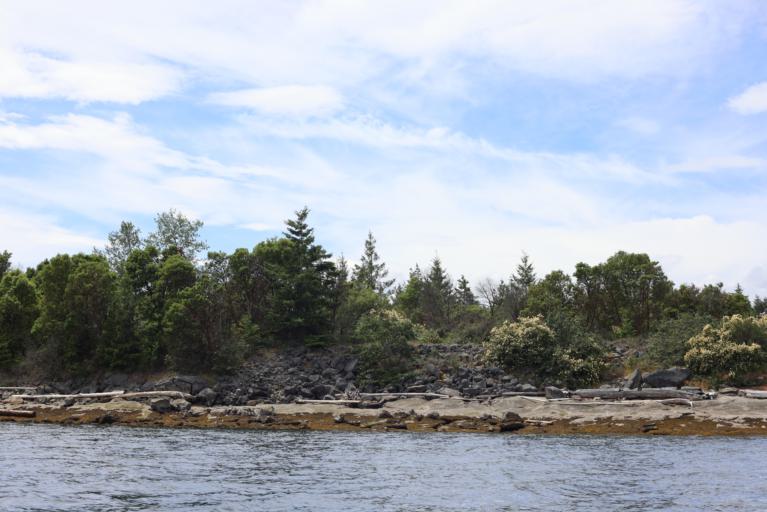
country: CA
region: British Columbia
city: Nanaimo
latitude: 49.1586
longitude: -123.8889
